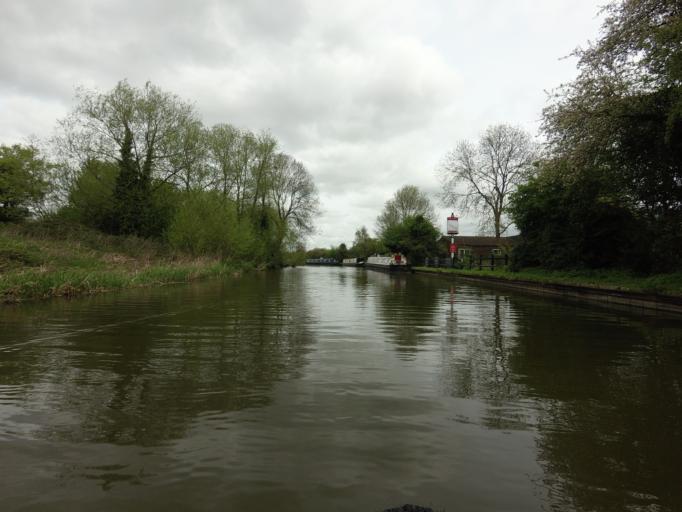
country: GB
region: England
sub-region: Milton Keynes
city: Simpson
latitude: 52.0167
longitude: -0.7185
